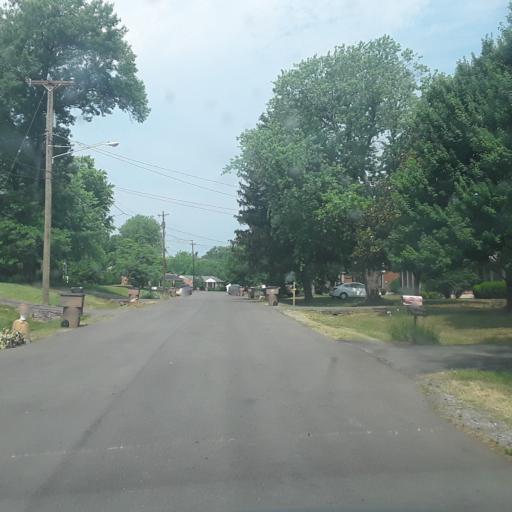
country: US
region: Tennessee
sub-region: Davidson County
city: Oak Hill
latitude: 36.0787
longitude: -86.7412
